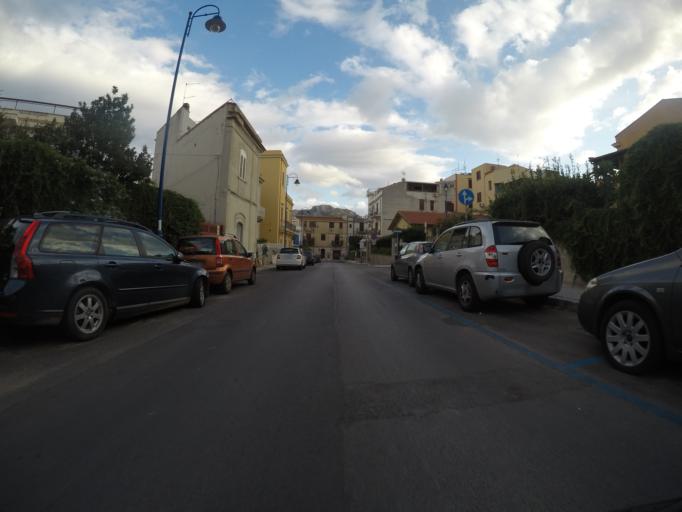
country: IT
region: Sicily
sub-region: Palermo
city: Palermo
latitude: 38.2090
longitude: 13.3272
